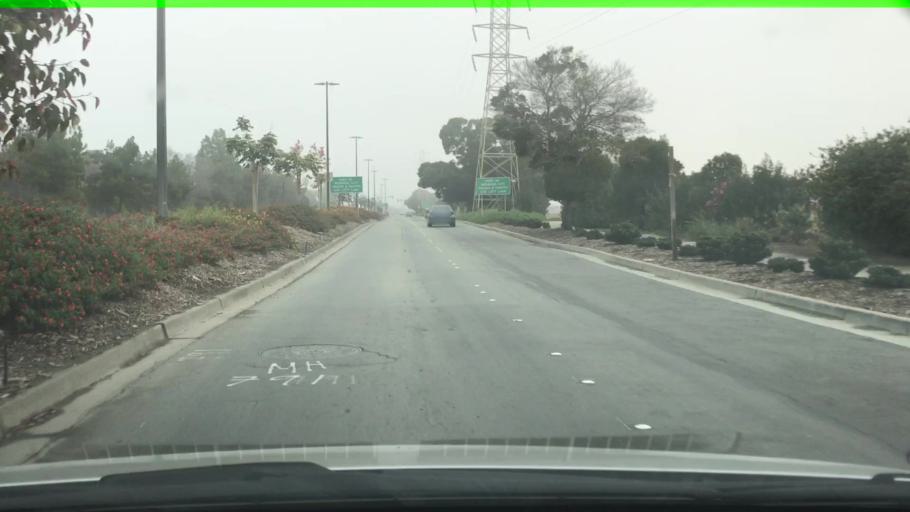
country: US
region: California
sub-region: San Mateo County
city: Redwood City
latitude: 37.4993
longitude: -122.2119
